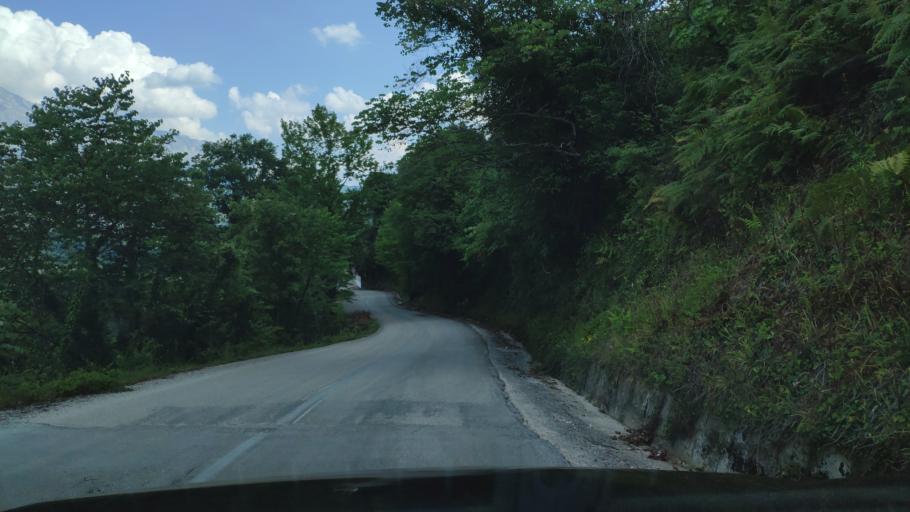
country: GR
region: Epirus
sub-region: Nomos Artas
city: Agios Dimitrios
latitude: 39.4620
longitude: 21.0249
